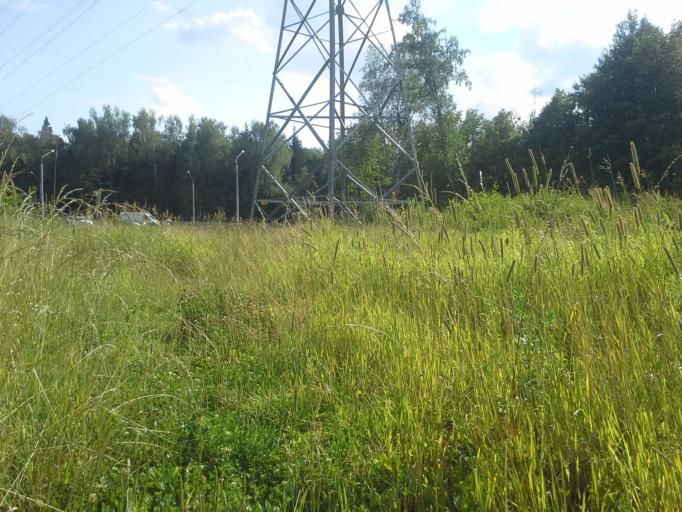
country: RU
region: Moskovskaya
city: Klimovsk
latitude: 55.3942
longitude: 37.5058
